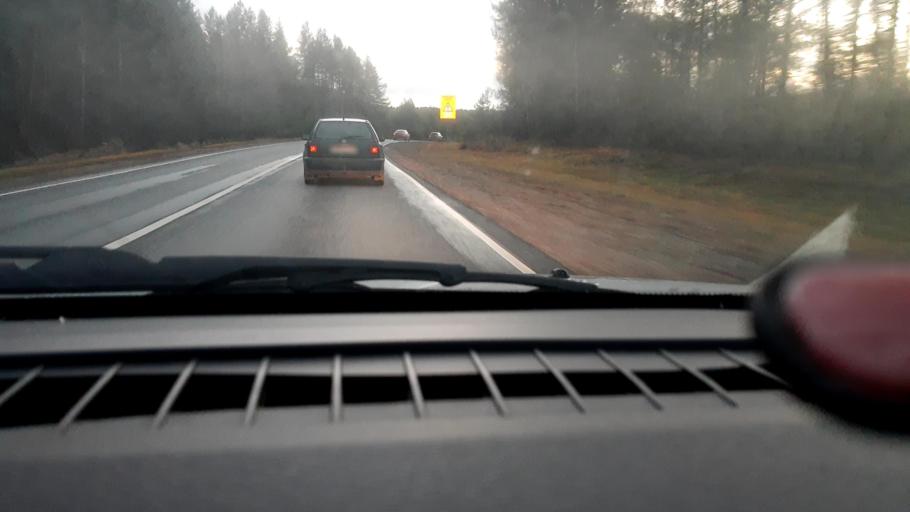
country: RU
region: Nizjnij Novgorod
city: Krasnyye Baki
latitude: 57.0325
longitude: 45.1206
